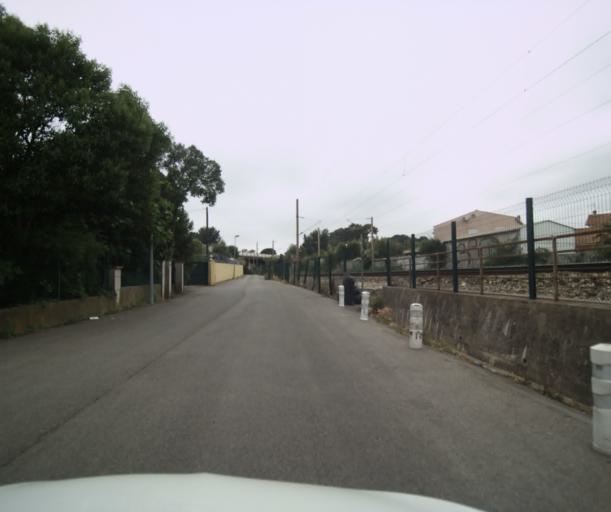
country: FR
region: Provence-Alpes-Cote d'Azur
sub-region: Departement du Var
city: La Seyne-sur-Mer
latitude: 43.1270
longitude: 5.8857
